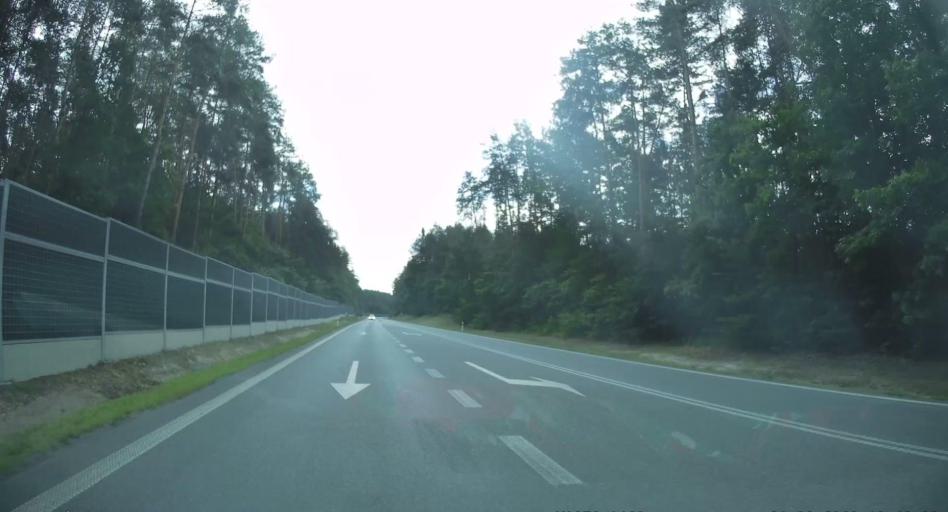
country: PL
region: Subcarpathian Voivodeship
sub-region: Powiat mielecki
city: Mielec
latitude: 50.2871
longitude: 21.4967
